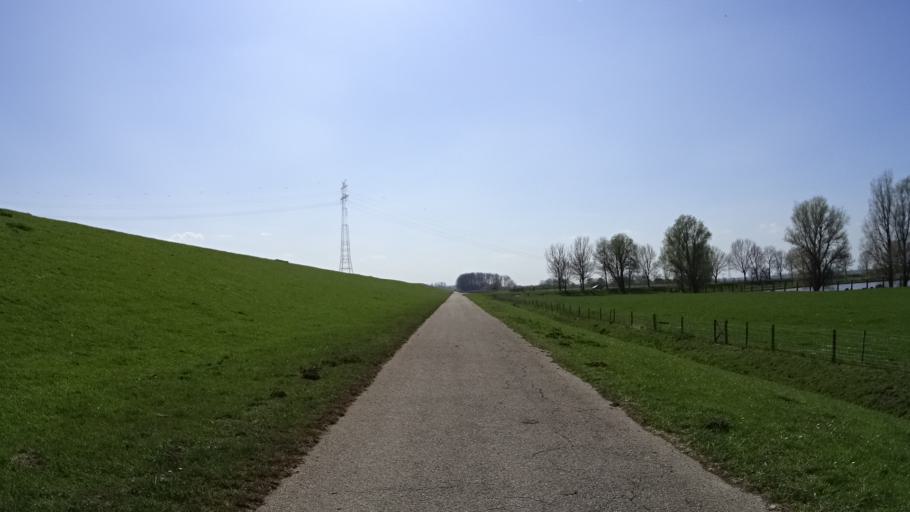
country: DE
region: Lower Saxony
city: Weener
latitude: 53.1526
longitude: 7.3712
